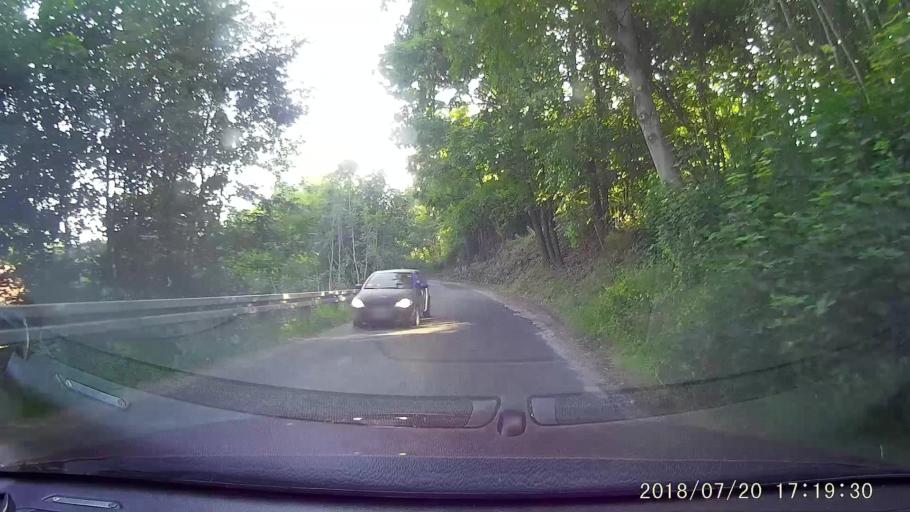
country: PL
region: Lower Silesian Voivodeship
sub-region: Powiat lubanski
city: Lesna
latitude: 50.9908
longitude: 15.2905
